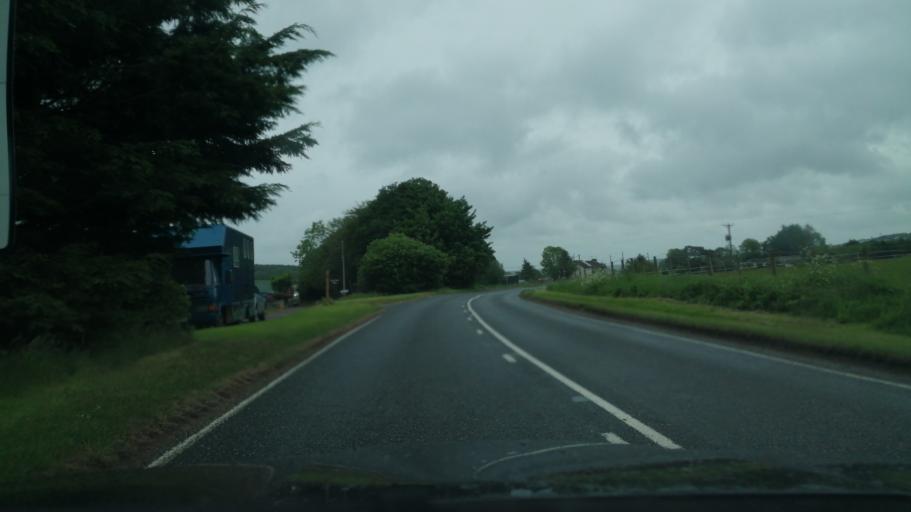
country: GB
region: Scotland
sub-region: Aberdeenshire
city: Portsoy
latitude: 57.5958
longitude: -2.7320
